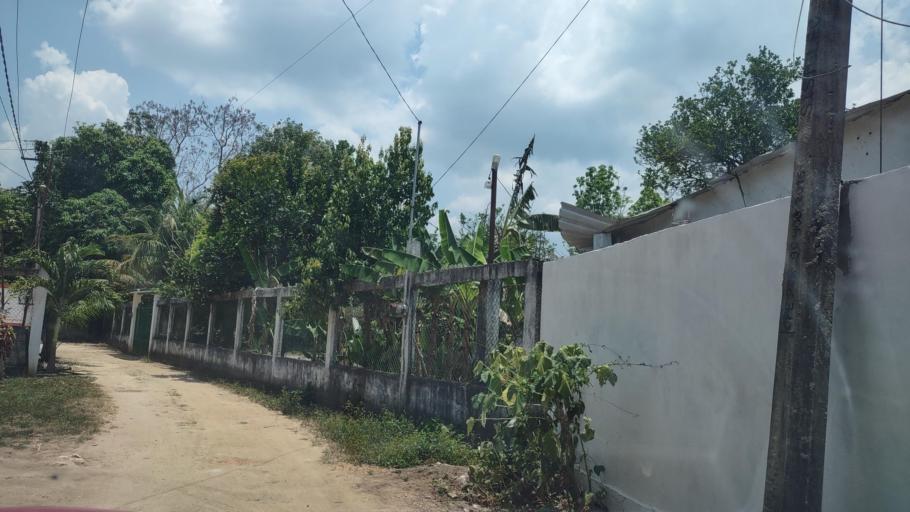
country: MX
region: Veracruz
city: Las Choapas
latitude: 17.9246
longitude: -94.0961
